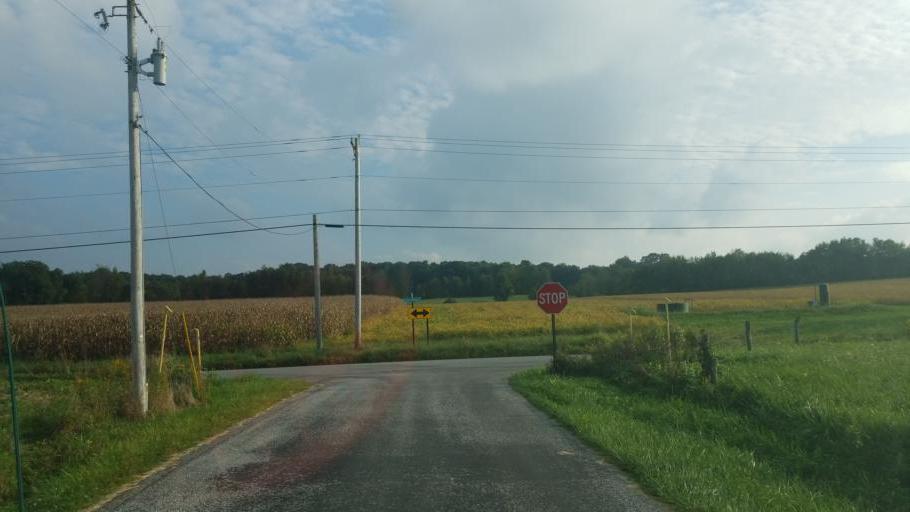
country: US
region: Ohio
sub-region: Wayne County
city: Wooster
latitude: 40.8583
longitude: -82.0293
